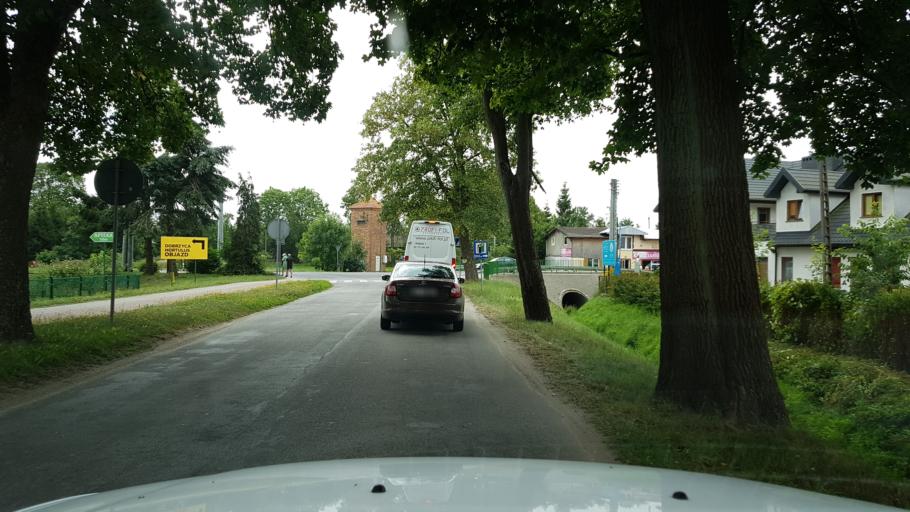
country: PL
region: West Pomeranian Voivodeship
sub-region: Powiat koszalinski
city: Mielno
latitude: 54.2102
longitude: 15.9904
